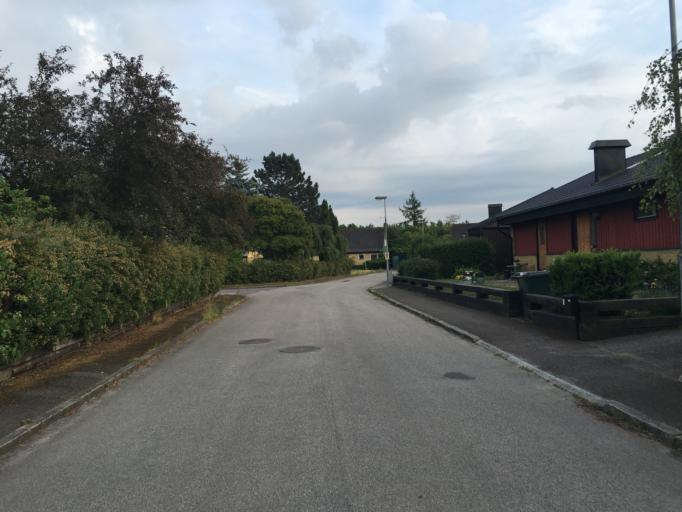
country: SE
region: Skane
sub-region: Lunds Kommun
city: Lund
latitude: 55.7467
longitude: 13.1937
